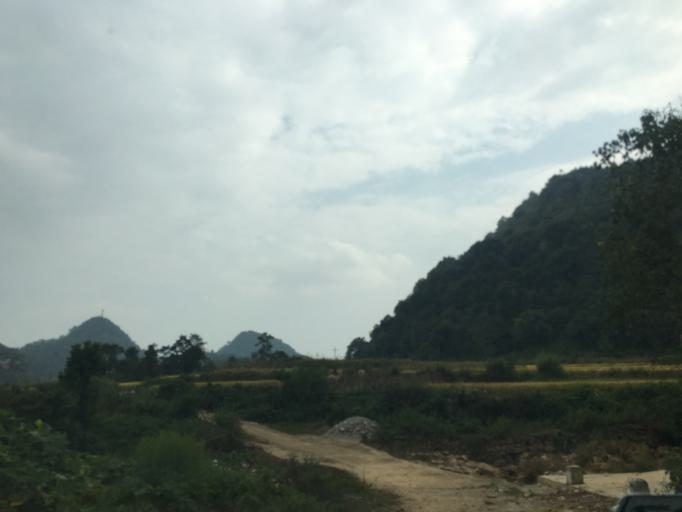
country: CN
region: Guangxi Zhuangzu Zizhiqu
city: Xinzhou
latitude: 25.4953
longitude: 105.6504
